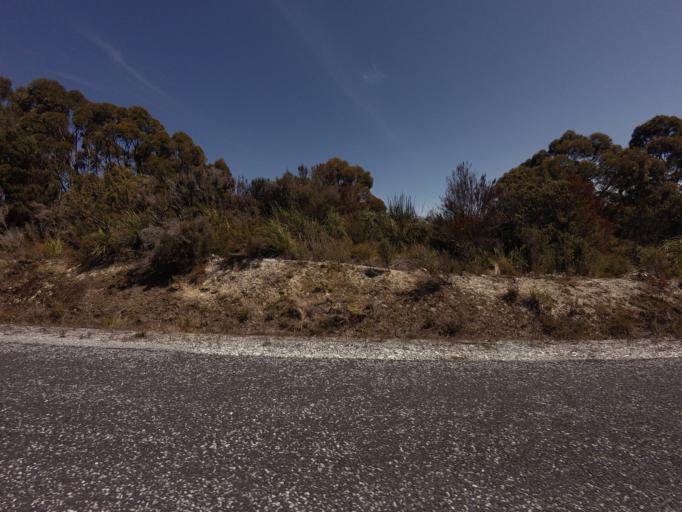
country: AU
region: Tasmania
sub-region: Huon Valley
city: Geeveston
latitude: -42.8349
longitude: 146.1385
